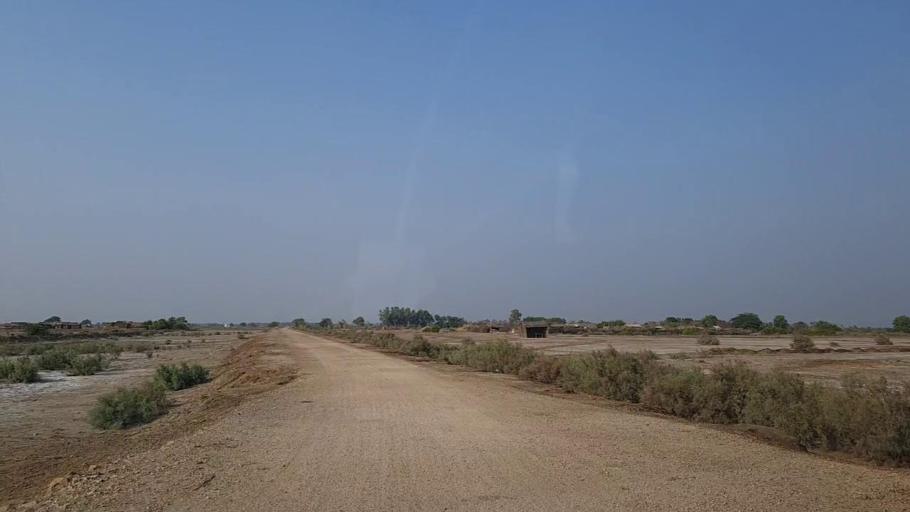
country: PK
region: Sindh
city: Mirpur Sakro
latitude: 24.6292
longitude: 67.7680
